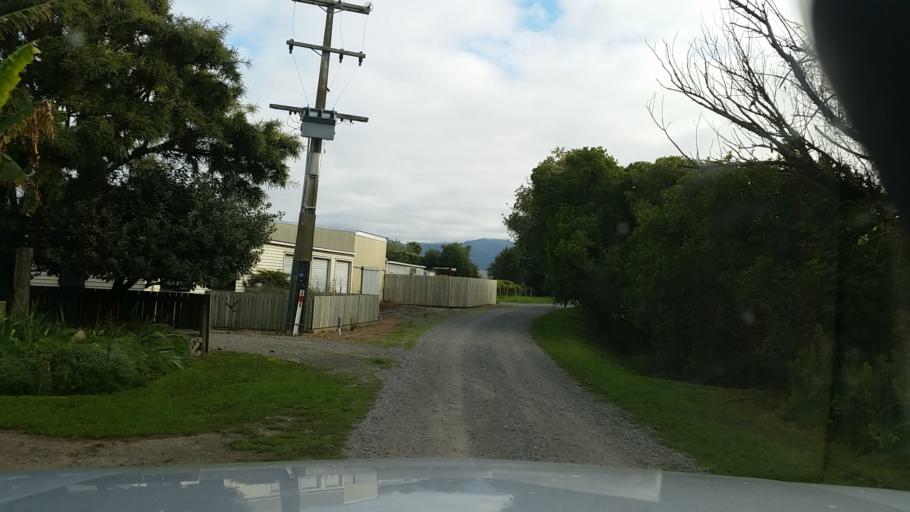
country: NZ
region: Marlborough
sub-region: Marlborough District
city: Blenheim
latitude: -41.4750
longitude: 173.9810
